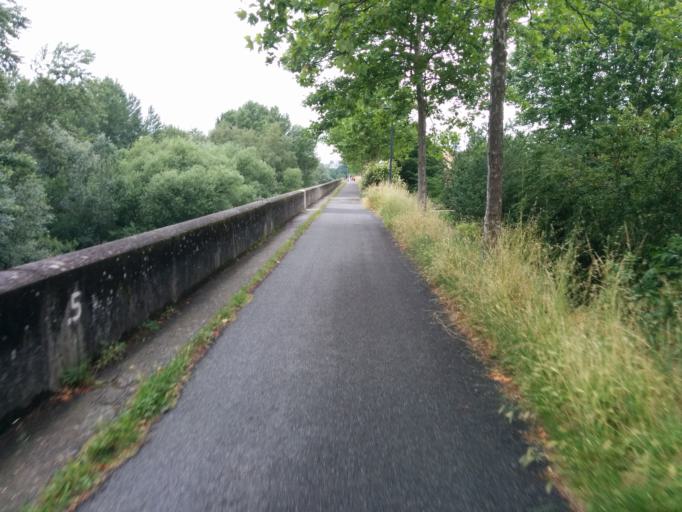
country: FR
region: Midi-Pyrenees
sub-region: Departement de la Haute-Garonne
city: Blagnac
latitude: 43.6124
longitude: 1.4089
